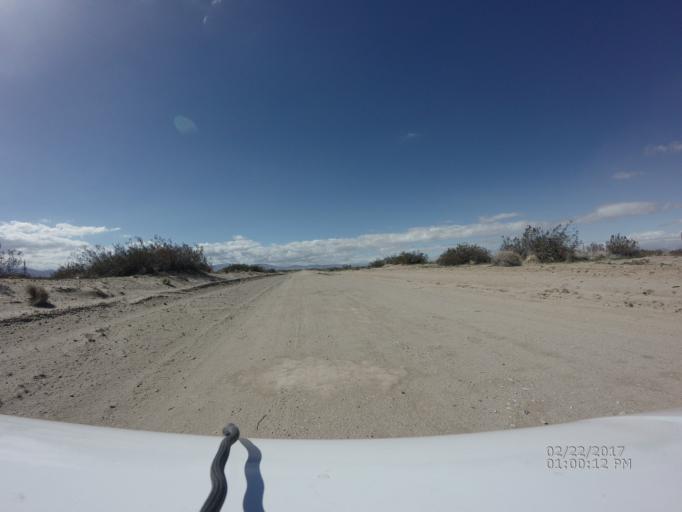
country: US
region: California
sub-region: Los Angeles County
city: Littlerock
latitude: 34.6017
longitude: -117.9528
